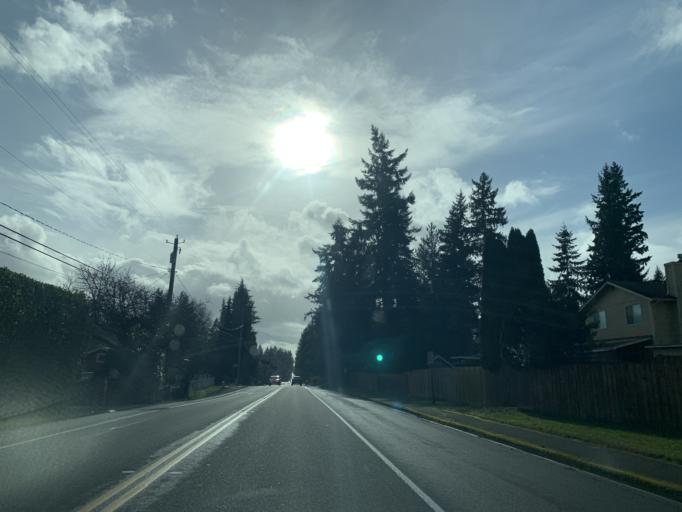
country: US
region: Washington
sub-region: King County
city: Lakeland South
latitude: 47.2842
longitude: -122.2977
